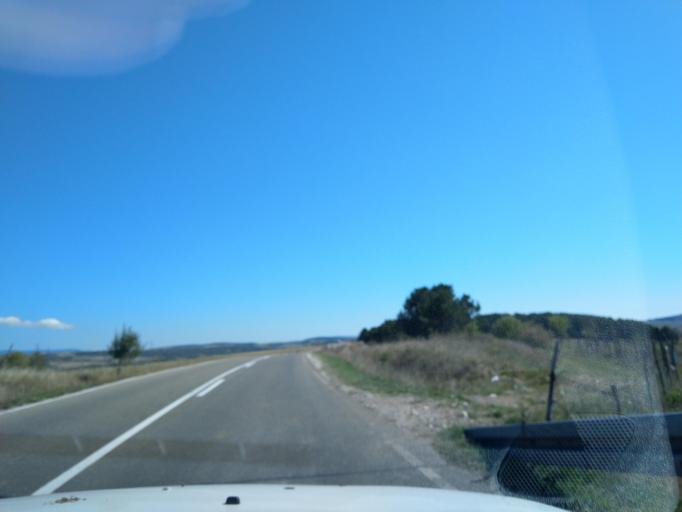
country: RS
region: Central Serbia
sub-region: Zlatiborski Okrug
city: Sjenica
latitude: 43.2659
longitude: 20.0399
